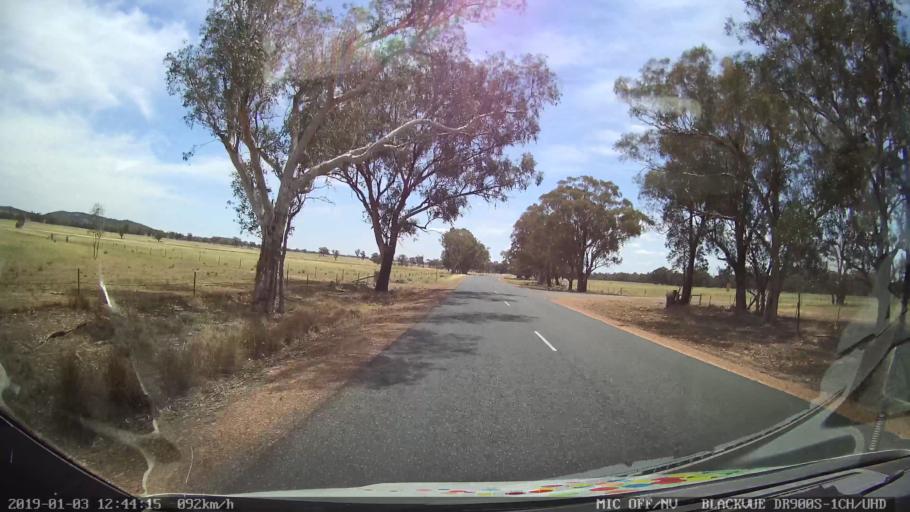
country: AU
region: New South Wales
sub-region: Weddin
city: Grenfell
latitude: -33.7640
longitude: 148.2151
